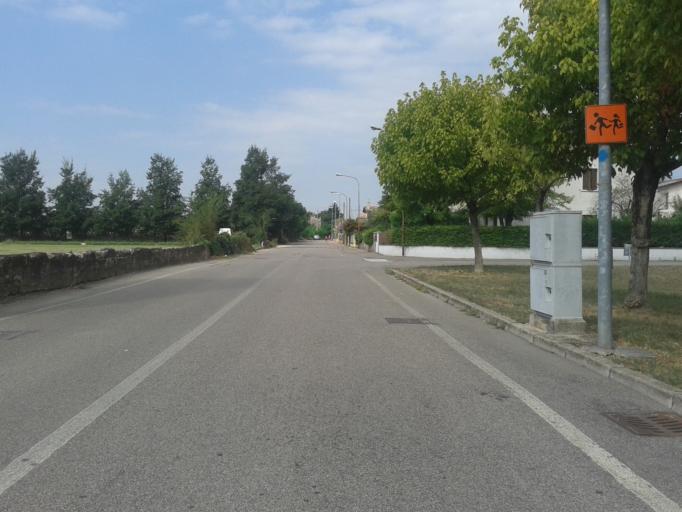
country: IT
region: Veneto
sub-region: Provincia di Verona
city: Mozzecane
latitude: 45.3051
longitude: 10.8133
